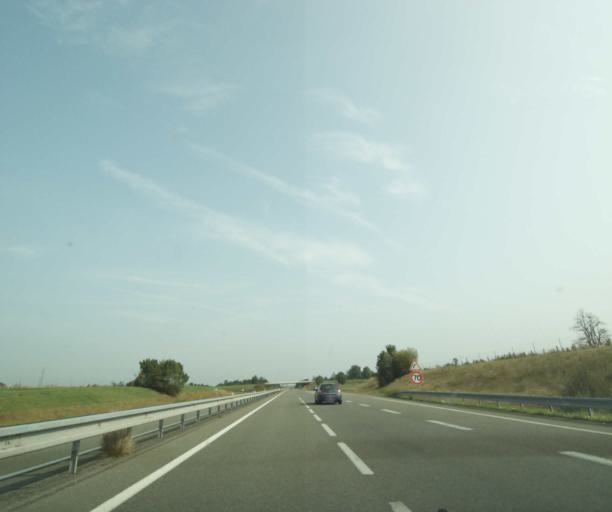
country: FR
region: Pays de la Loire
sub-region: Departement de la Sarthe
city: Montbizot
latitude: 48.1906
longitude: 0.1713
